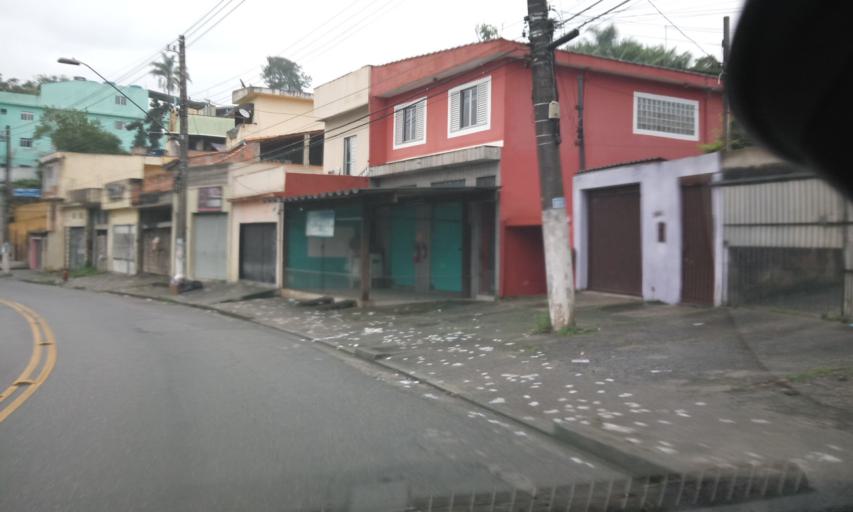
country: BR
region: Sao Paulo
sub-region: Maua
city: Maua
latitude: -23.7420
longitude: -46.4945
